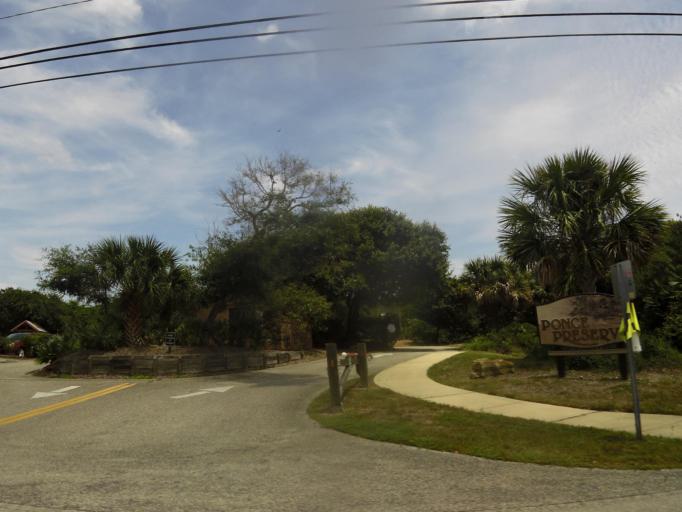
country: US
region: Florida
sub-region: Volusia County
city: Ponce Inlet
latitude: 29.1136
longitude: -80.9496
